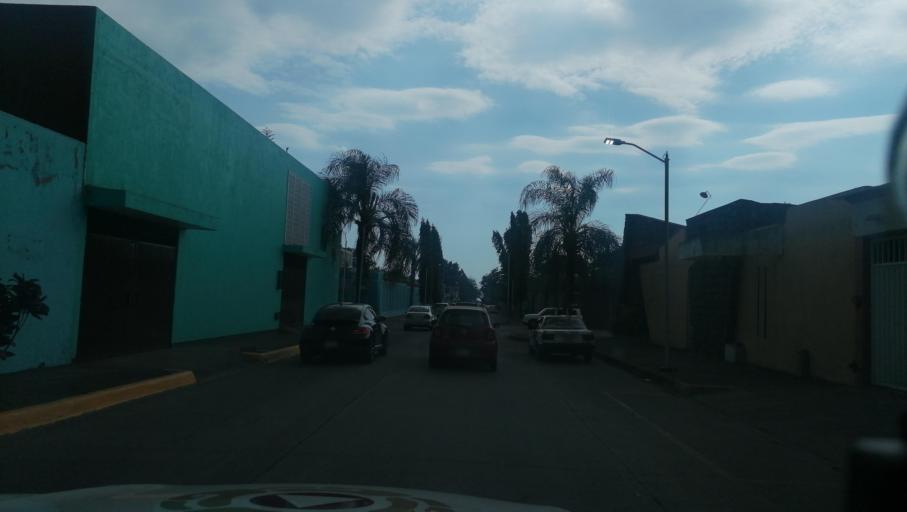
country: MX
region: Chiapas
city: Tapachula
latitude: 14.9167
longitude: -92.2531
